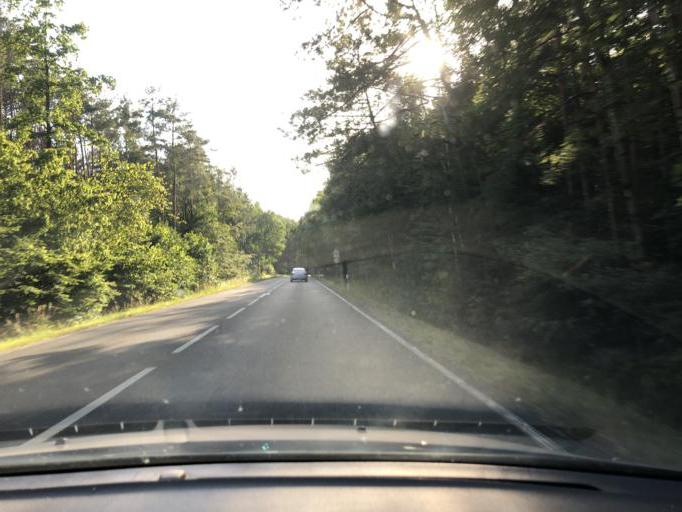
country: DE
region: Saxony
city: Falkenhain
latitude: 51.3343
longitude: 12.8888
